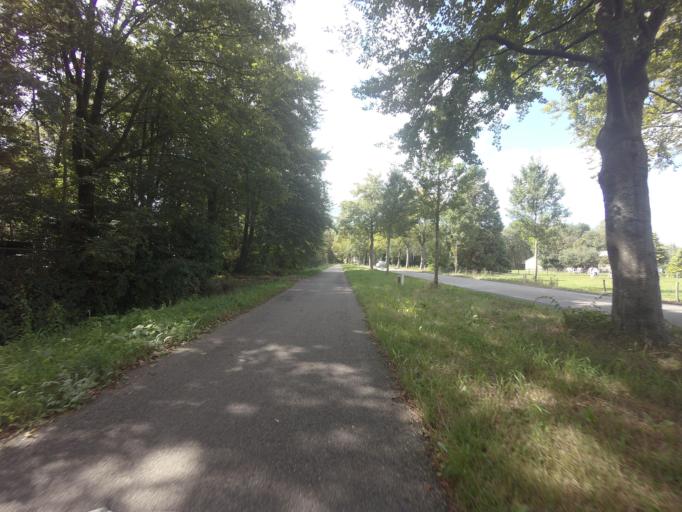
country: NL
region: Drenthe
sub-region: Gemeente Westerveld
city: Dwingeloo
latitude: 52.9549
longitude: 6.3242
